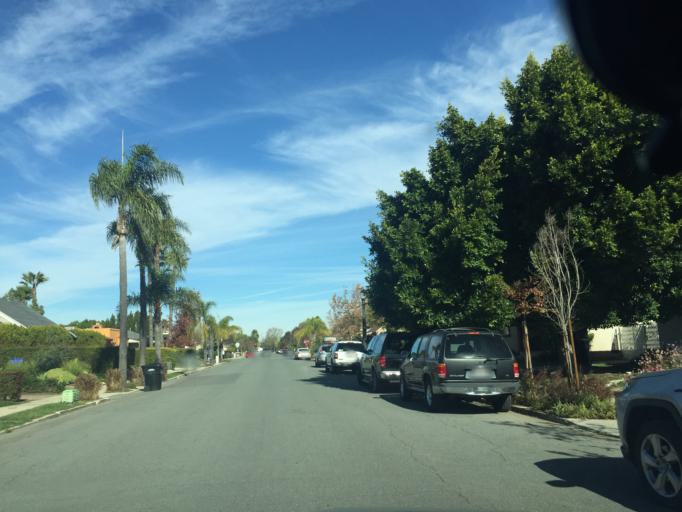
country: US
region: California
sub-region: San Diego County
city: Lemon Grove
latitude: 32.7619
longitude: -117.0878
